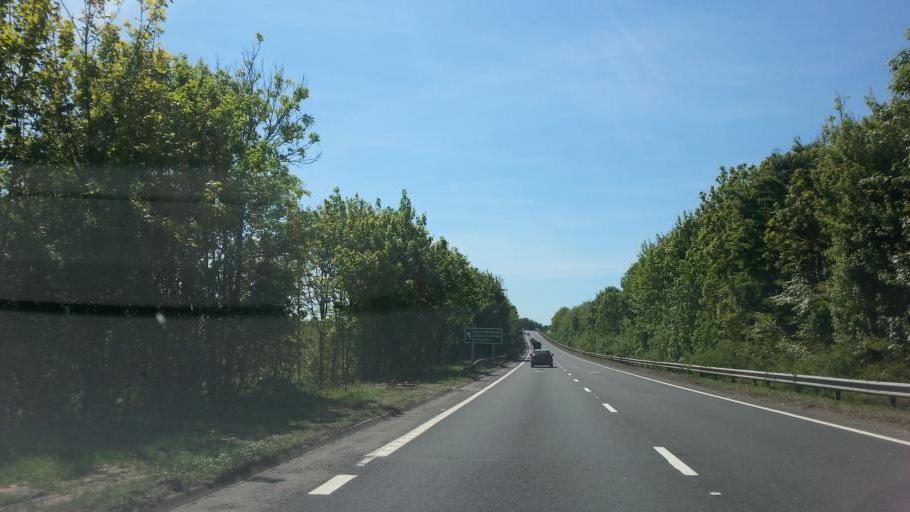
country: GB
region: England
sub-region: Hampshire
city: Kings Worthy
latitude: 51.1765
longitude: -1.3261
